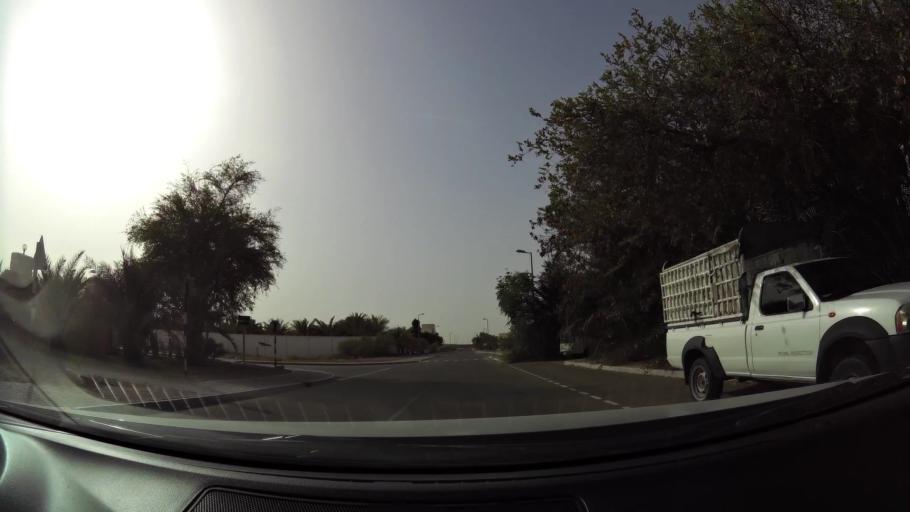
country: AE
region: Abu Dhabi
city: Al Ain
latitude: 24.1993
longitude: 55.6110
